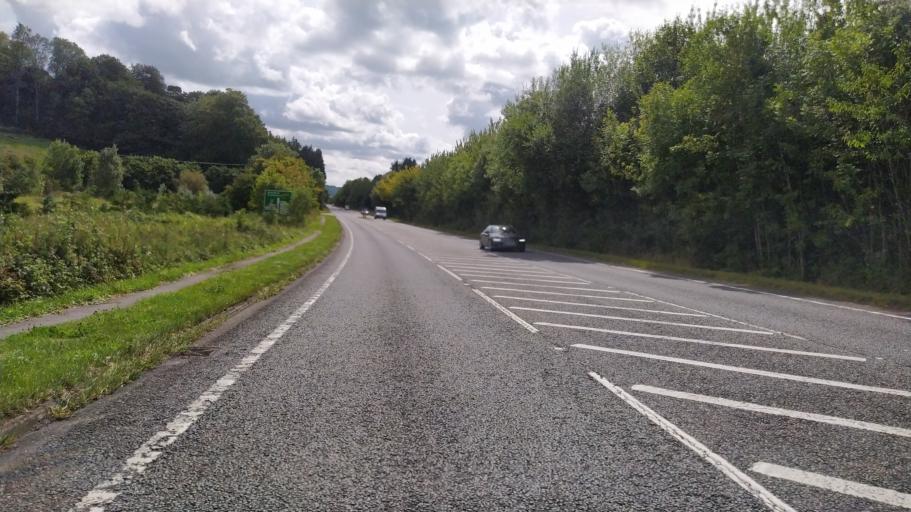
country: GB
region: England
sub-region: Wiltshire
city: Hindon
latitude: 51.0785
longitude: -2.1679
